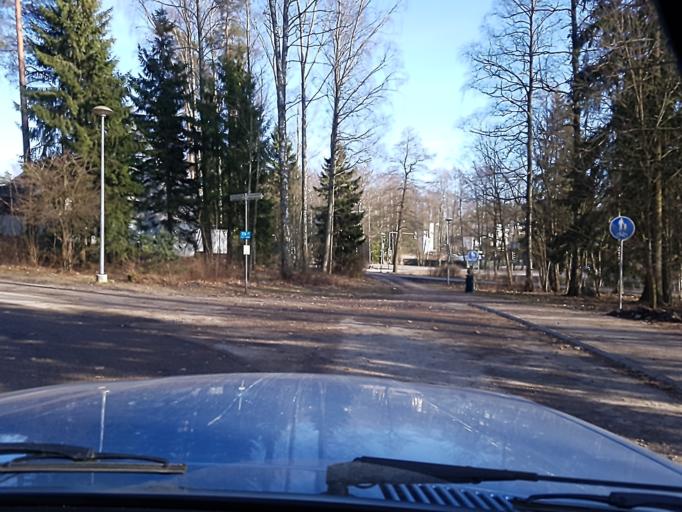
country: FI
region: Uusimaa
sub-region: Helsinki
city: Koukkuniemi
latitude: 60.1743
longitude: 24.7875
